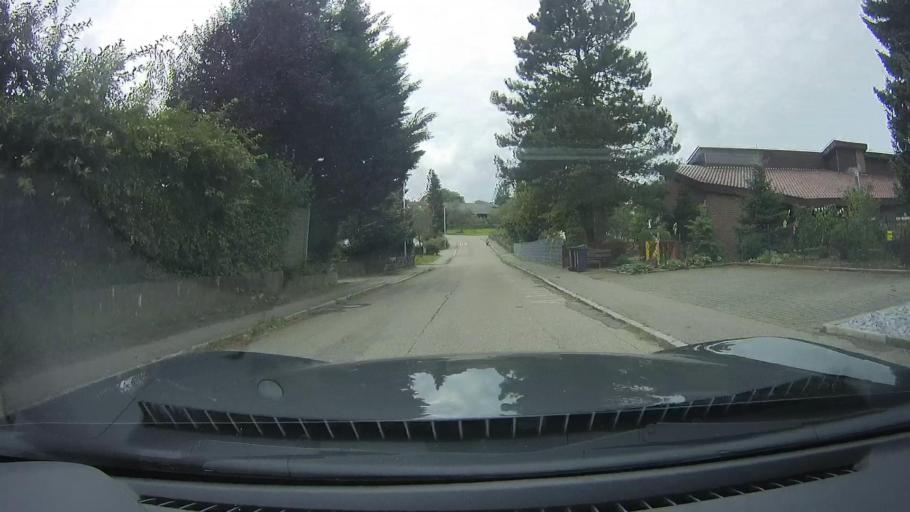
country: DE
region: Baden-Wuerttemberg
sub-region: Regierungsbezirk Stuttgart
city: Althutte
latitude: 48.9448
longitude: 9.5508
